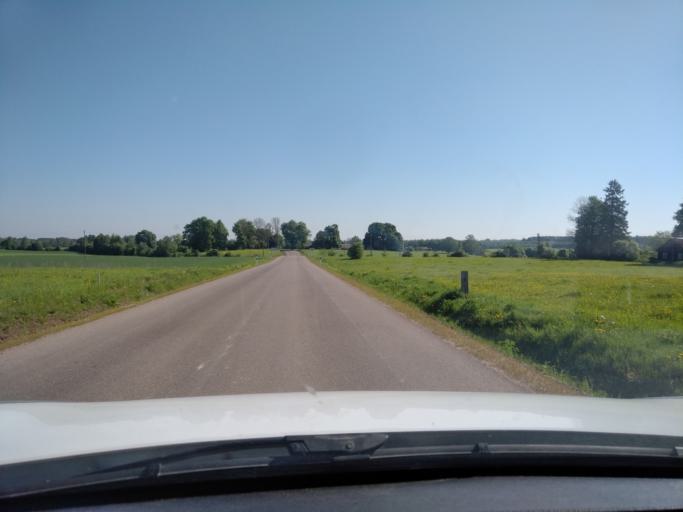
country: LT
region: Utenos apskritis
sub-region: Utena
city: Utena
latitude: 55.6700
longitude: 25.5001
